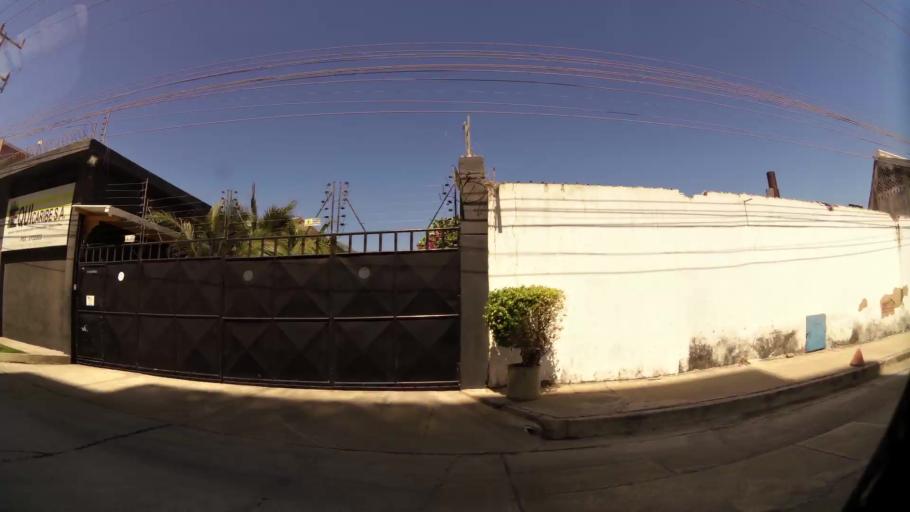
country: CO
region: Atlantico
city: Barranquilla
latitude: 11.0180
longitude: -74.8015
